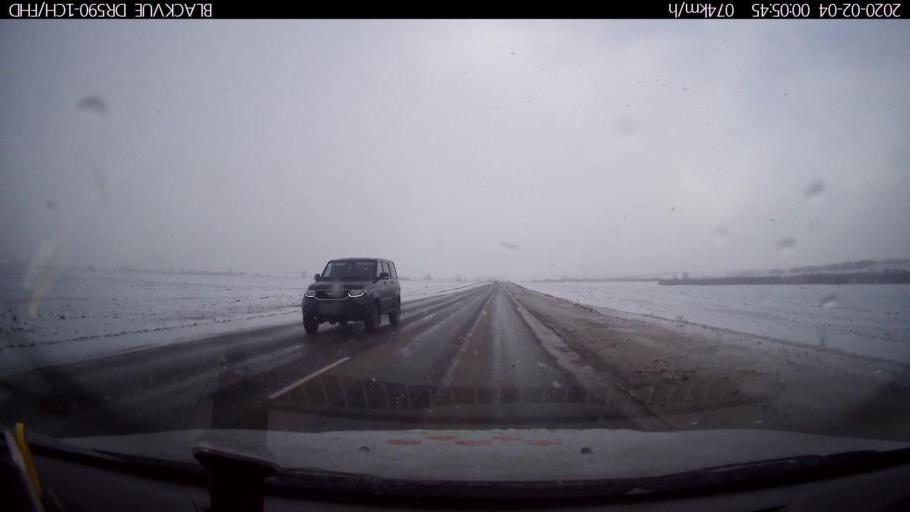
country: RU
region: Nizjnij Novgorod
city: Dal'neye Konstantinovo
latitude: 55.8403
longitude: 44.1260
